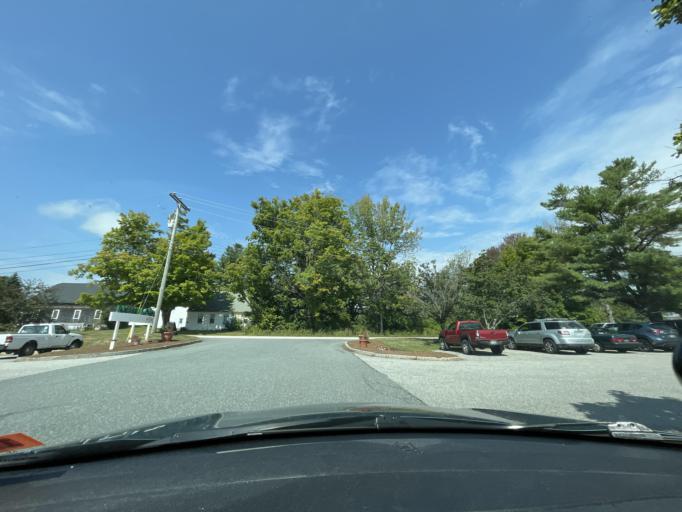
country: US
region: New Hampshire
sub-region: Merrimack County
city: New London
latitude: 43.4212
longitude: -72.0008
